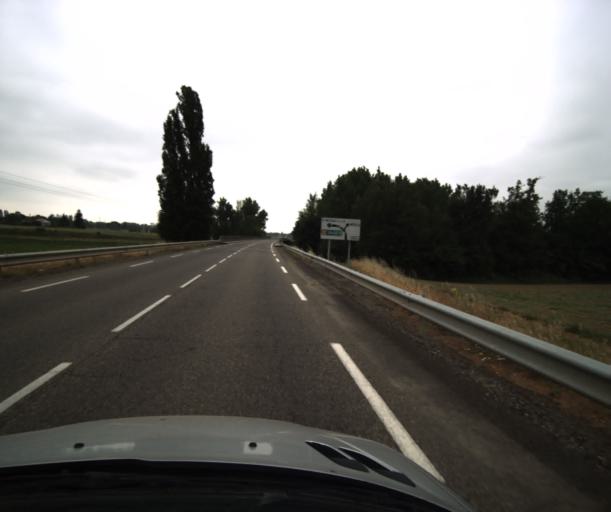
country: FR
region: Midi-Pyrenees
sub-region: Departement du Tarn-et-Garonne
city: Saint-Nicolas-de-la-Grave
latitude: 44.0775
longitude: 0.9944
